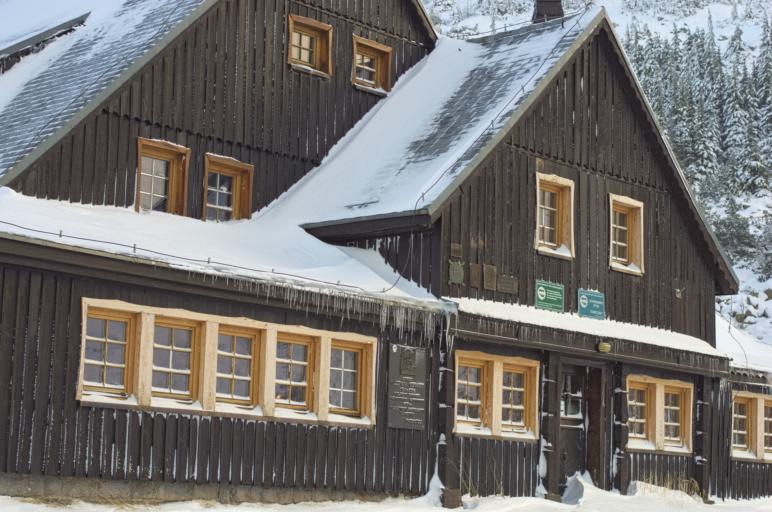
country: PL
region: Lower Silesian Voivodeship
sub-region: Powiat jeleniogorski
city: Karpacz
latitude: 50.7489
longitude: 15.7022
